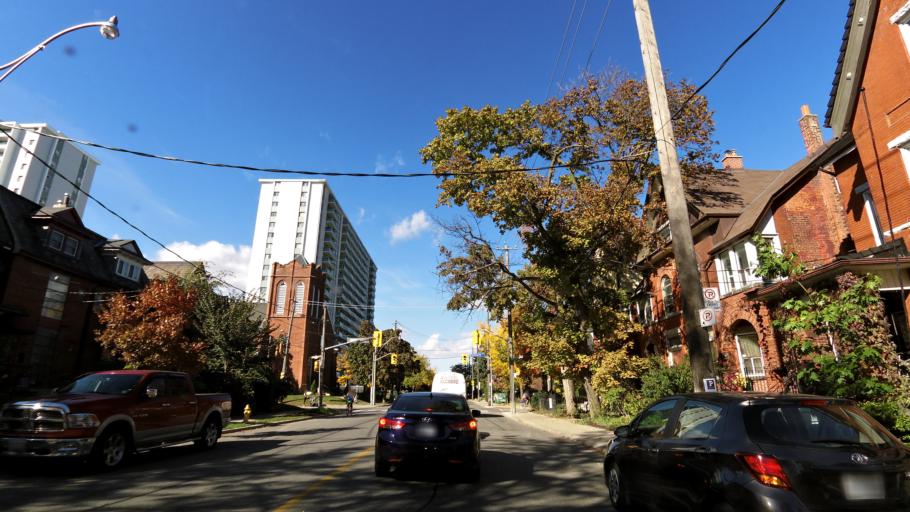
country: CA
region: Ontario
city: Toronto
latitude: 43.6586
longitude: -79.4283
